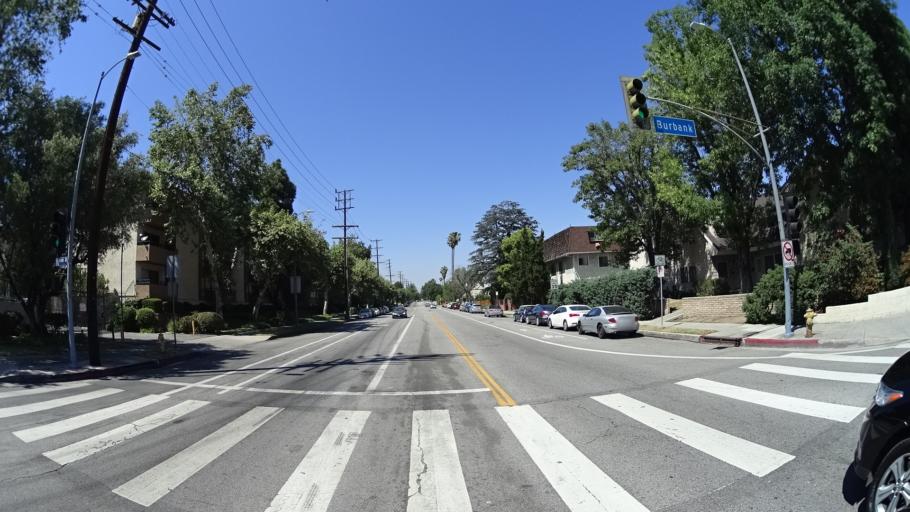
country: US
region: California
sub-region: Los Angeles County
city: North Hollywood
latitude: 34.1723
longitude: -118.3878
